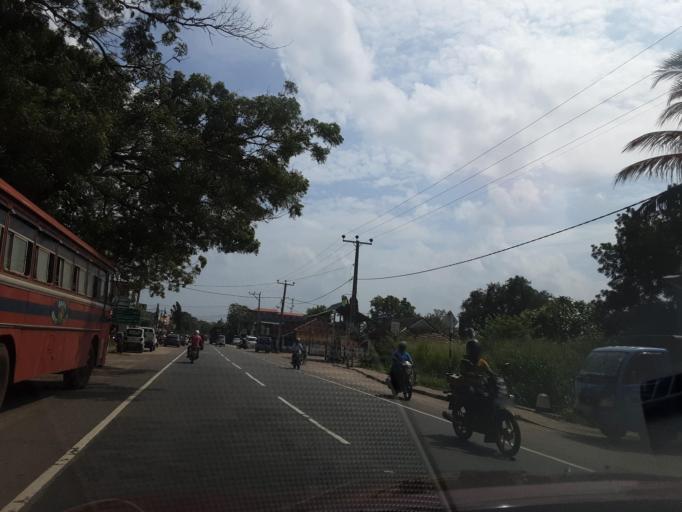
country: LK
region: Northern Province
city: Vavuniya
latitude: 8.5348
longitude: 80.4956
